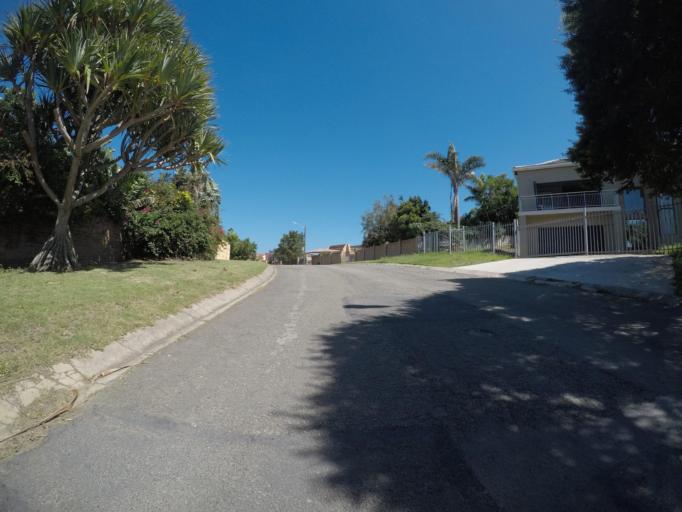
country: ZA
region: Eastern Cape
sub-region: Buffalo City Metropolitan Municipality
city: East London
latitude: -32.9791
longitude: 27.9361
